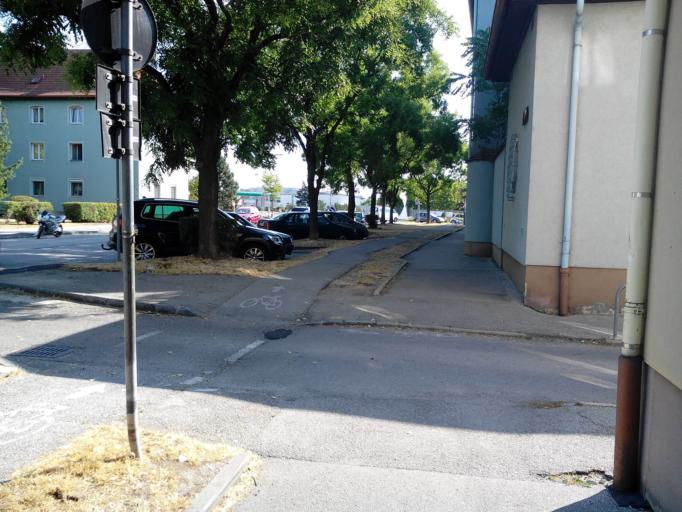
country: AT
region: Lower Austria
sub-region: Politischer Bezirk Wiener Neustadt
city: Theresienfeld
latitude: 47.8269
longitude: 16.2431
